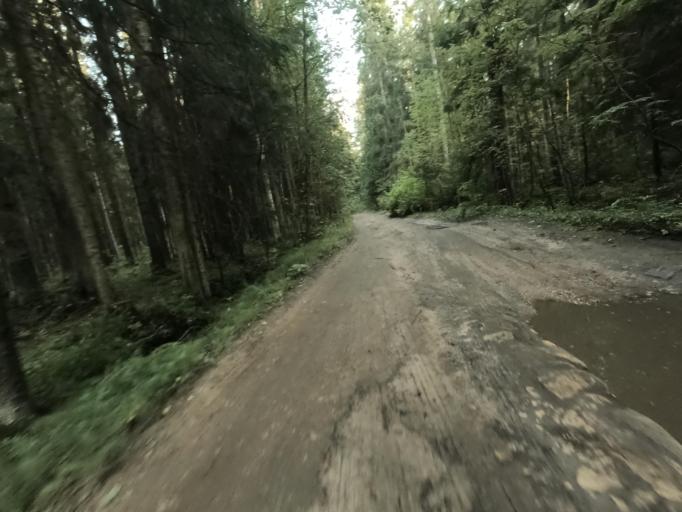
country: RU
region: Leningrad
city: Otradnoye
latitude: 59.8266
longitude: 30.7722
